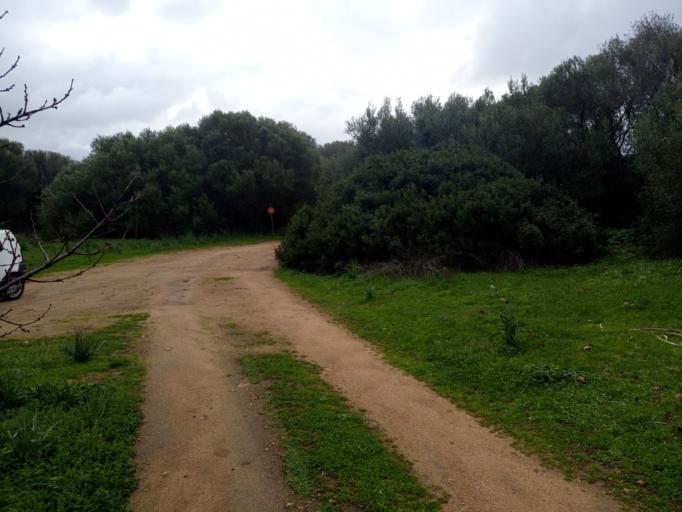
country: FR
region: Corsica
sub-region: Departement de la Corse-du-Sud
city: Sartene
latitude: 41.5463
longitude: 8.8925
